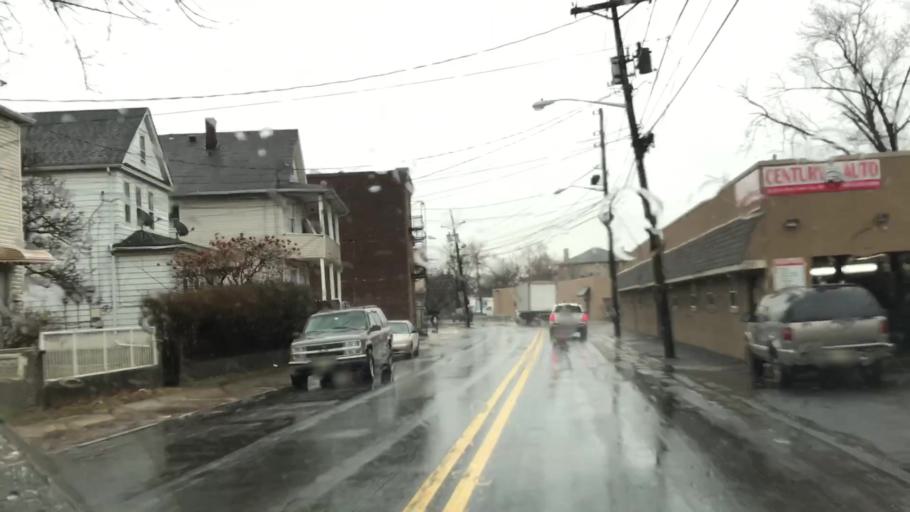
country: US
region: New Jersey
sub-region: Bergen County
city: Wallington
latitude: 40.8665
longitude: -74.1109
